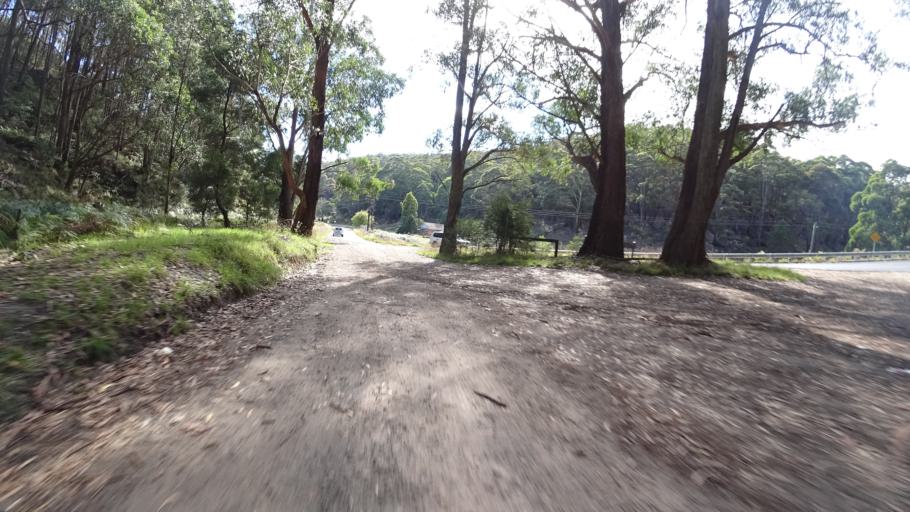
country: AU
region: New South Wales
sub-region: Lithgow
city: Lithgow
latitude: -33.5000
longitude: 150.1702
